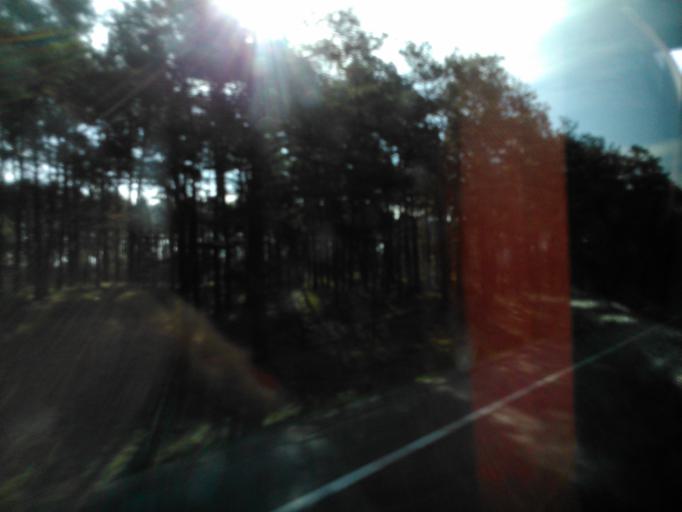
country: PL
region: Kujawsko-Pomorskie
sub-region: Powiat aleksandrowski
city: Aleksandrow Kujawski
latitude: 52.9518
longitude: 18.6923
